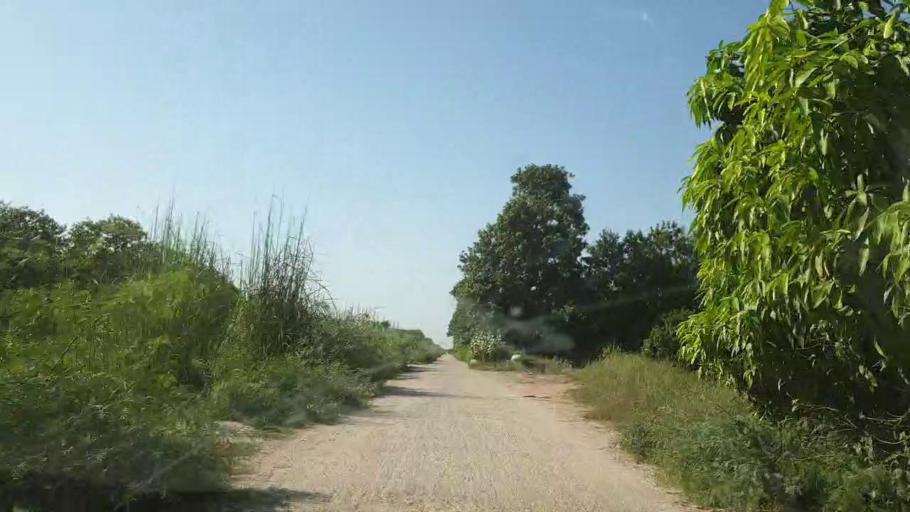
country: PK
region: Sindh
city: Tando Jam
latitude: 25.3303
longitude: 68.5903
